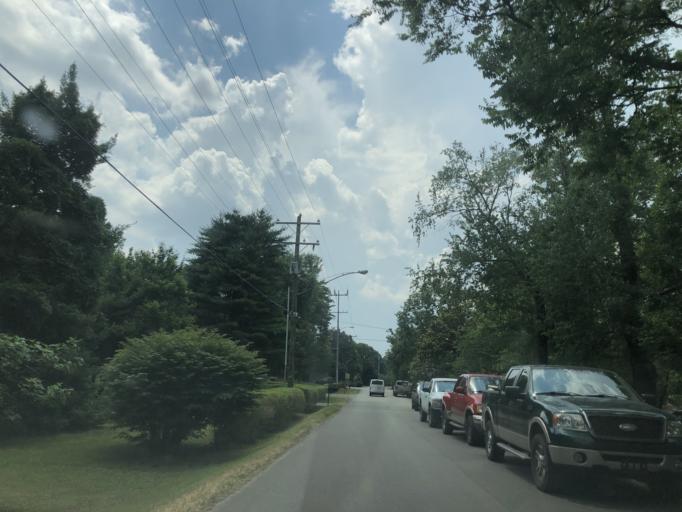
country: US
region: Tennessee
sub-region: Davidson County
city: Belle Meade
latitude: 36.1174
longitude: -86.8251
